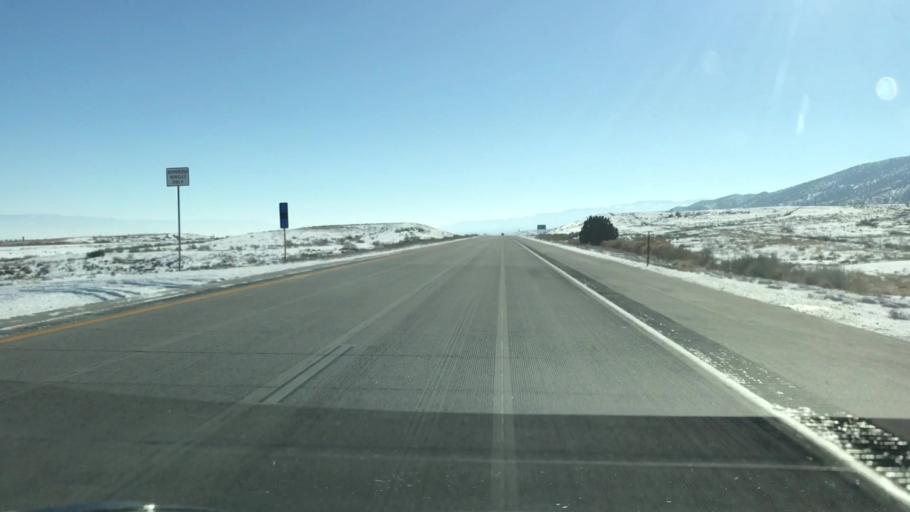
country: US
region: Colorado
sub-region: Mesa County
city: Loma
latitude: 39.2060
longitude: -108.8586
